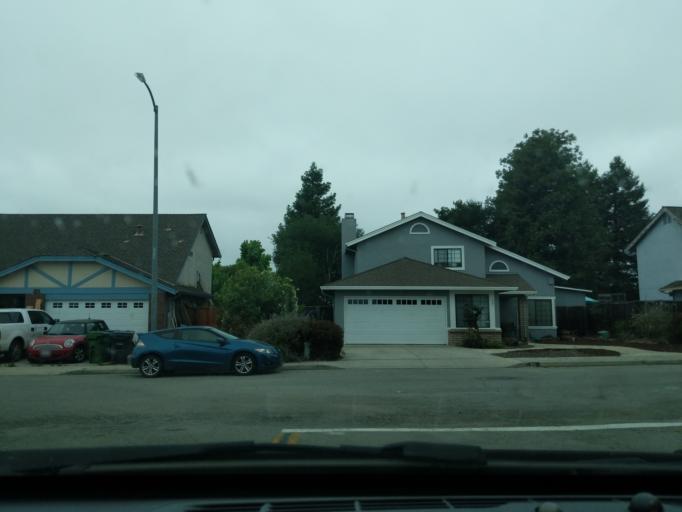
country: US
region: California
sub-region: Santa Cruz County
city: Interlaken
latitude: 36.9342
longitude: -121.7322
